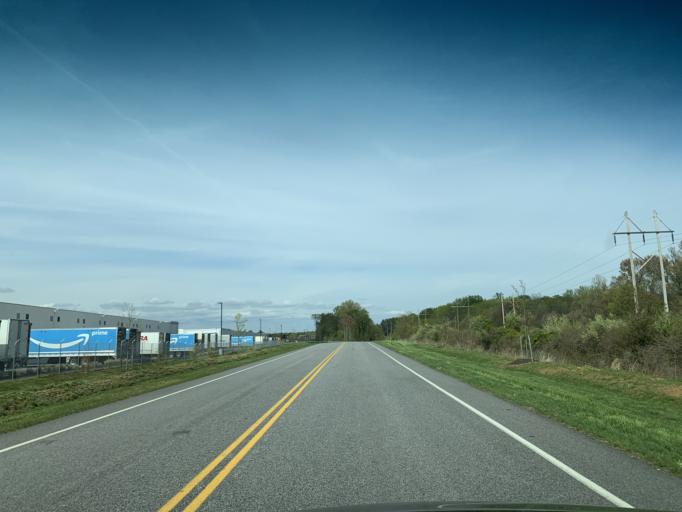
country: US
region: Maryland
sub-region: Harford County
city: Perryman
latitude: 39.4792
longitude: -76.1822
